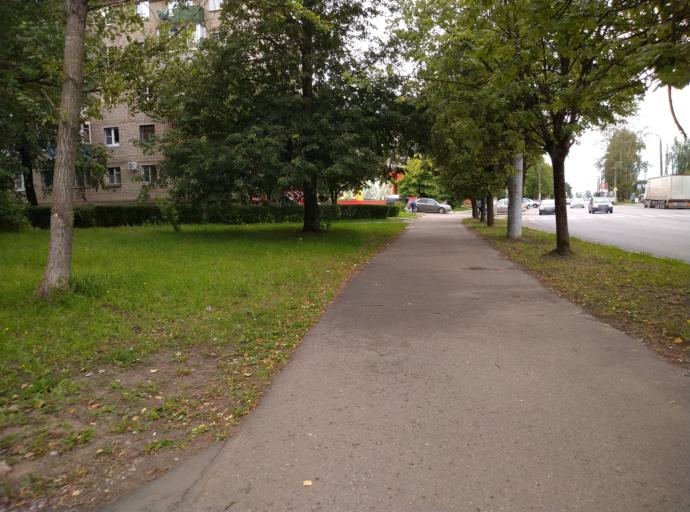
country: RU
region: Kostroma
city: Oktyabr'skiy
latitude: 57.7476
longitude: 40.9687
